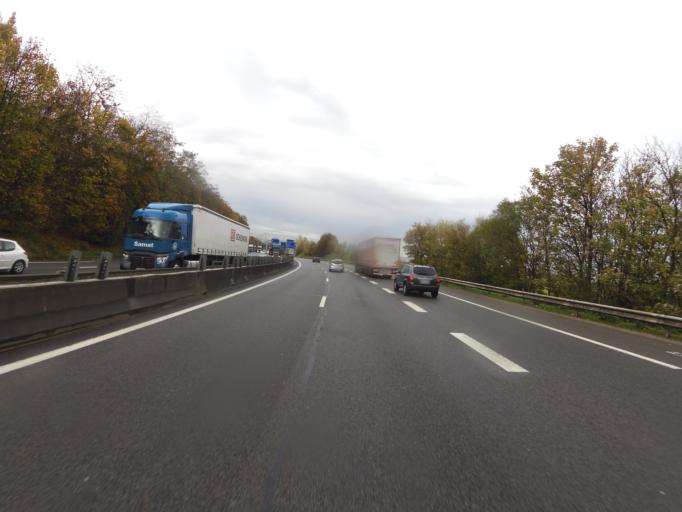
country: FR
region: Rhone-Alpes
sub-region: Departement du Rhone
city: Saint-Priest
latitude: 45.6965
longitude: 4.9696
